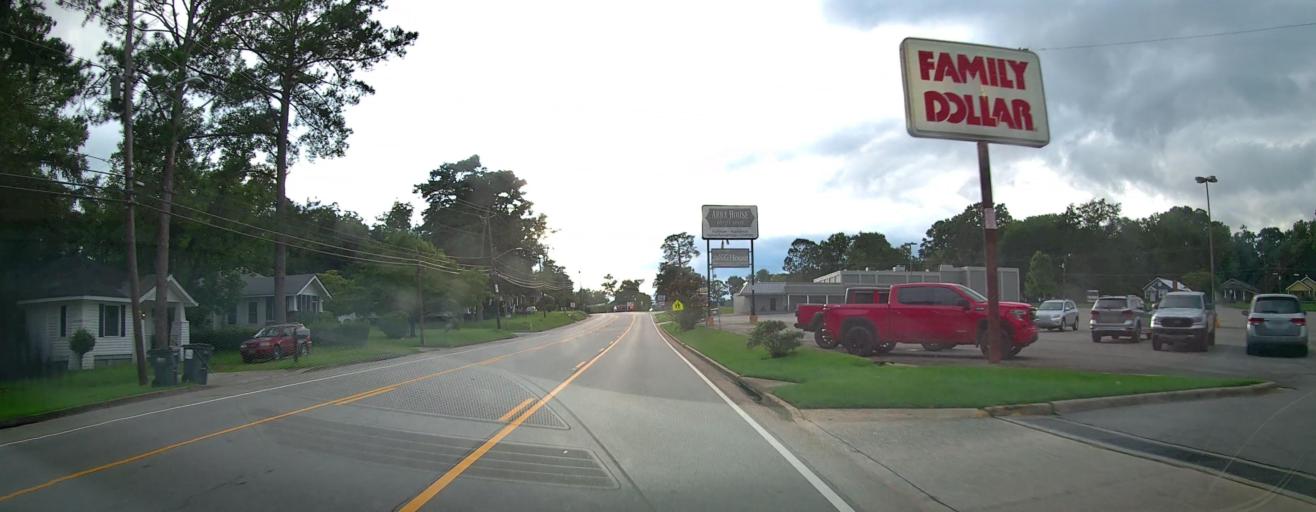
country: US
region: Georgia
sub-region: Houston County
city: Perry
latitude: 32.4593
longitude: -83.7240
